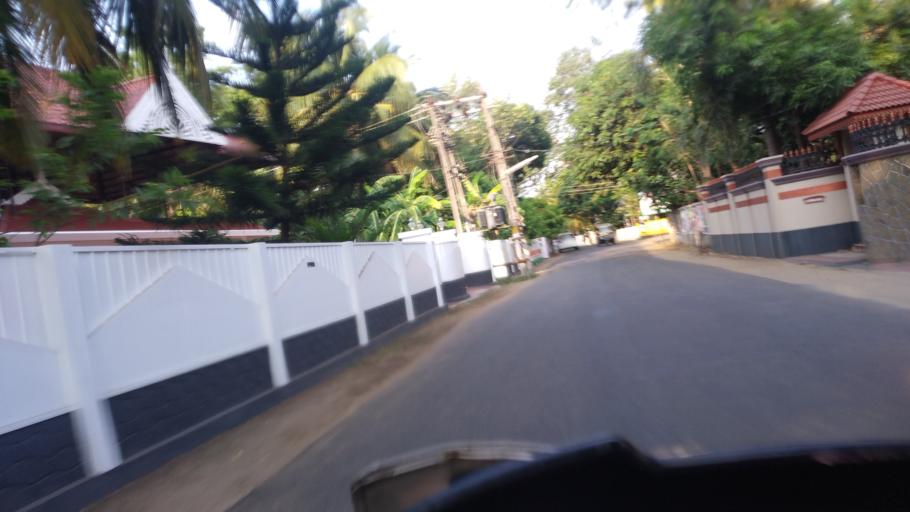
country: IN
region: Kerala
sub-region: Thrissur District
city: Thanniyam
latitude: 10.4391
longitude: 76.0882
